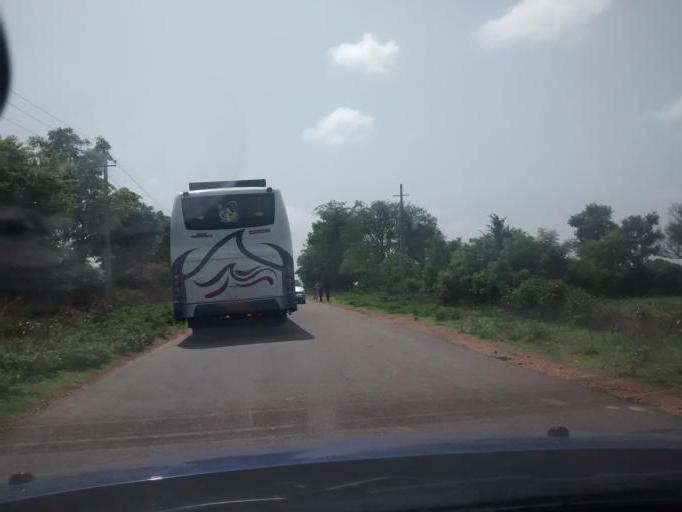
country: IN
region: Karnataka
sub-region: Hassan
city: Konanur
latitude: 12.5819
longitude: 76.1898
